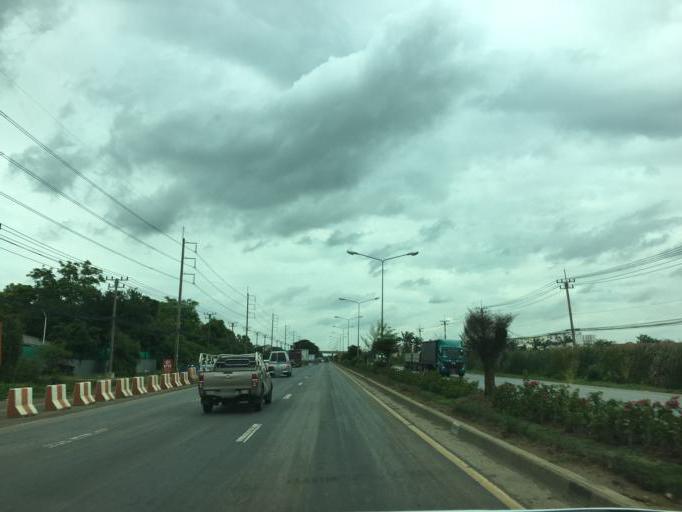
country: TH
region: Phra Nakhon Si Ayutthaya
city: Wang Noi
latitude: 14.2653
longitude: 100.6899
